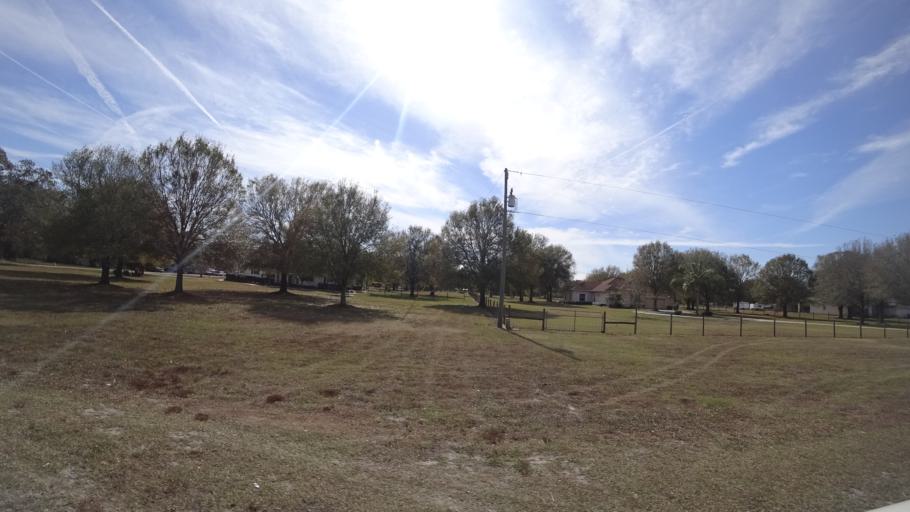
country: US
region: Florida
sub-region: Manatee County
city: Ellenton
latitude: 27.5758
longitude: -82.4059
